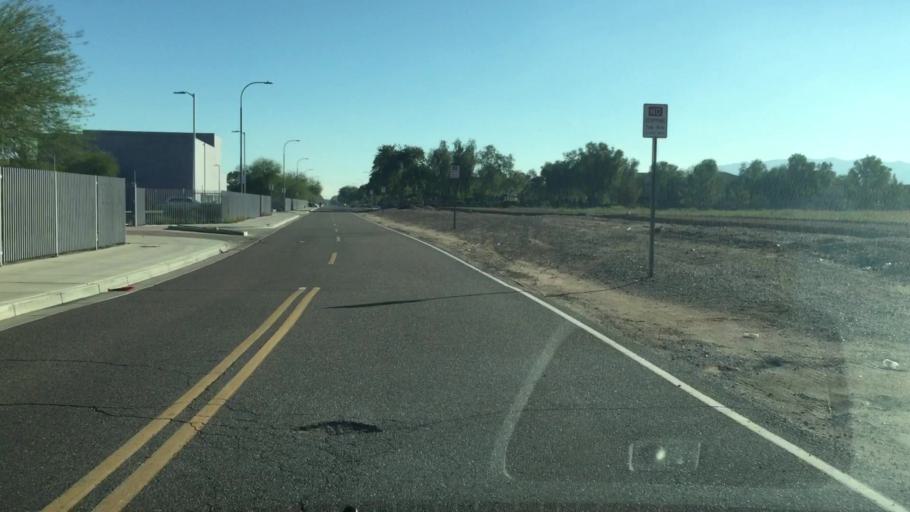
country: US
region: Arizona
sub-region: Maricopa County
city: Laveen
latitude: 33.3702
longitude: -112.1836
